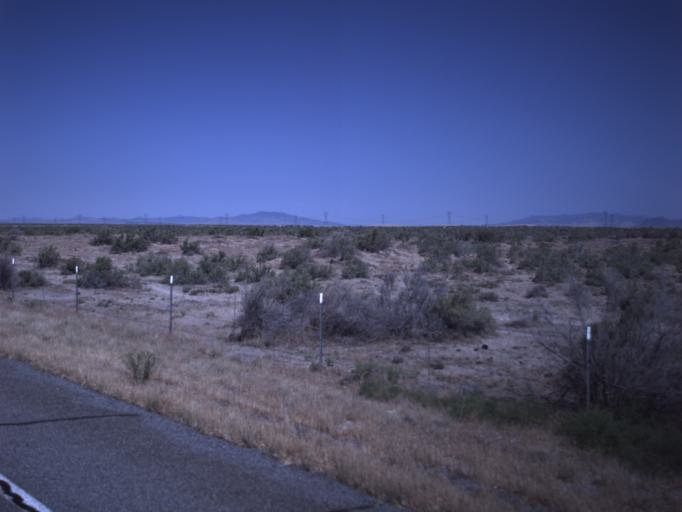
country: US
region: Utah
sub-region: Millard County
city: Delta
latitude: 39.4712
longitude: -112.4649
